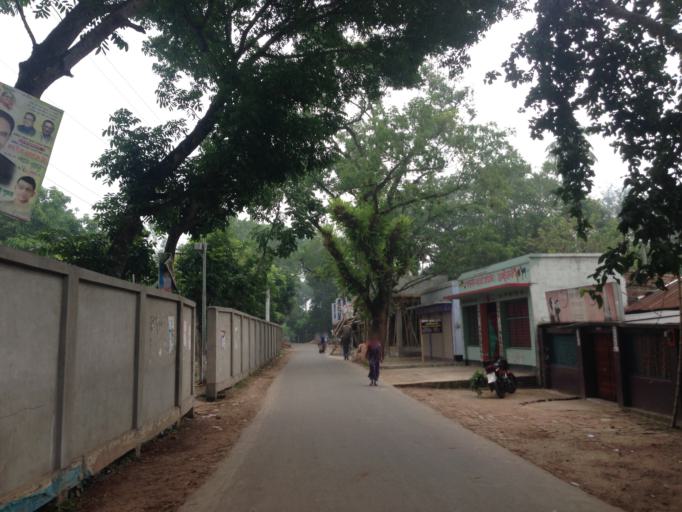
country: BD
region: Khulna
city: Kalia
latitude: 23.0410
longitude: 89.6333
